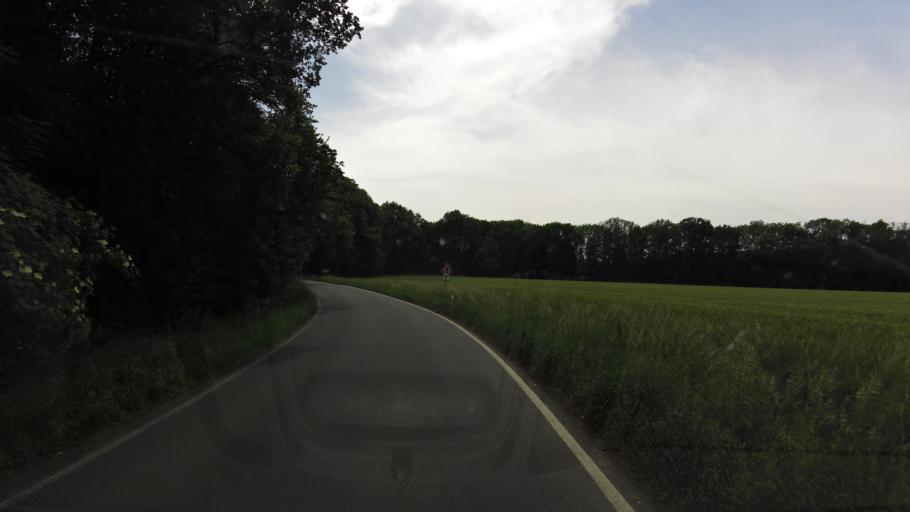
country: CZ
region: Plzensky
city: Prestice
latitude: 49.5928
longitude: 13.3949
